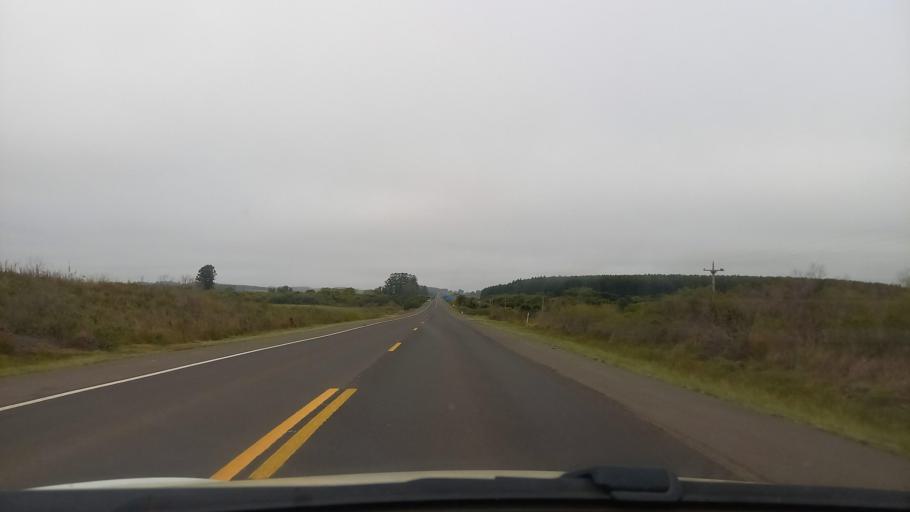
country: BR
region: Rio Grande do Sul
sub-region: Rosario Do Sul
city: Rosario do Sul
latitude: -30.2898
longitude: -54.9857
